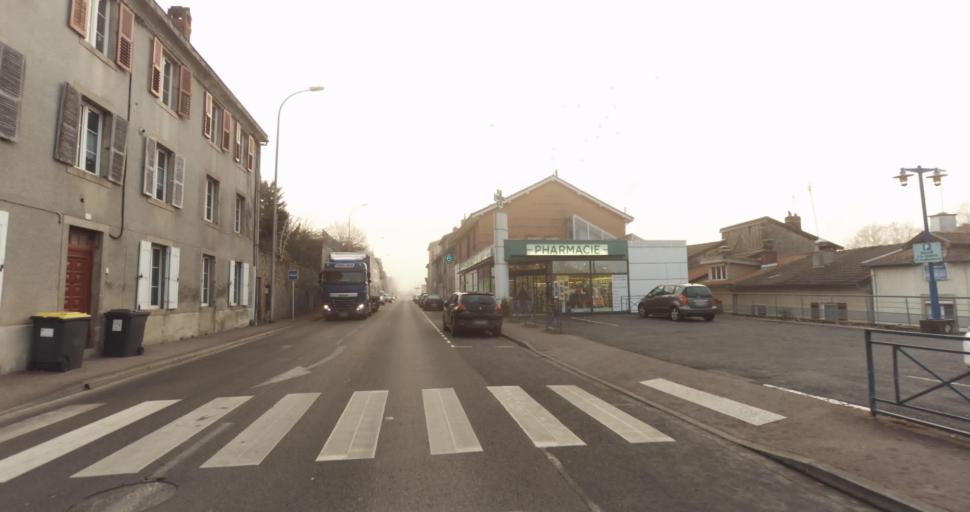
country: FR
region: Limousin
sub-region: Departement de la Haute-Vienne
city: Aixe-sur-Vienne
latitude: 45.7975
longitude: 1.1448
